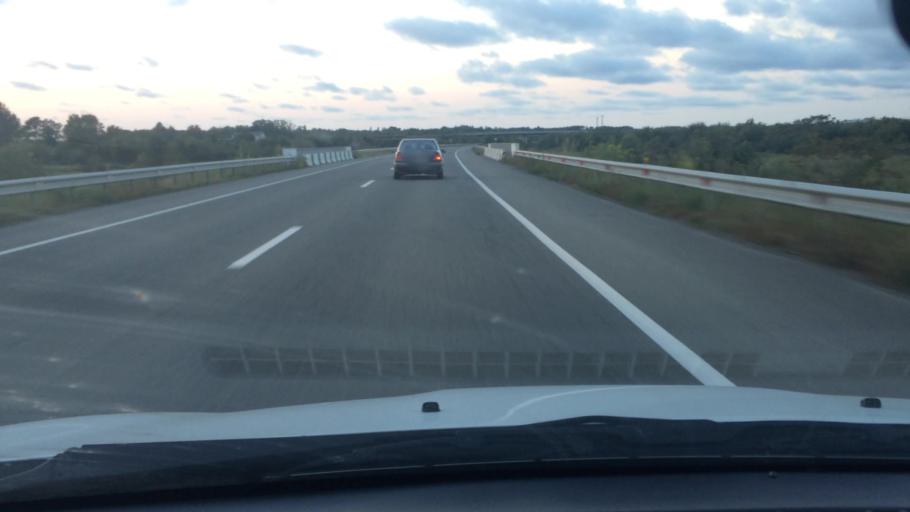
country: GE
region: Guria
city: Urek'i
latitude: 41.9132
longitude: 41.7796
